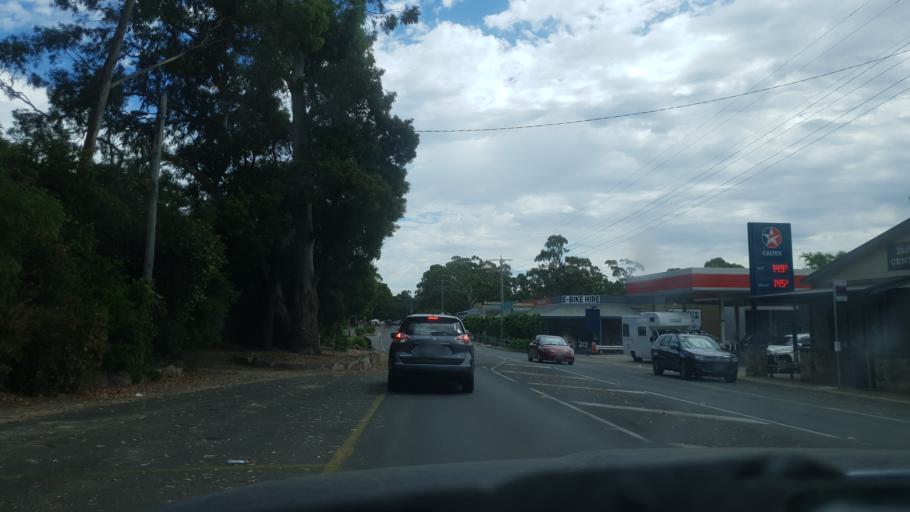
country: AU
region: Victoria
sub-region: Northern Grampians
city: Stawell
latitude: -37.1406
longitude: 142.5190
